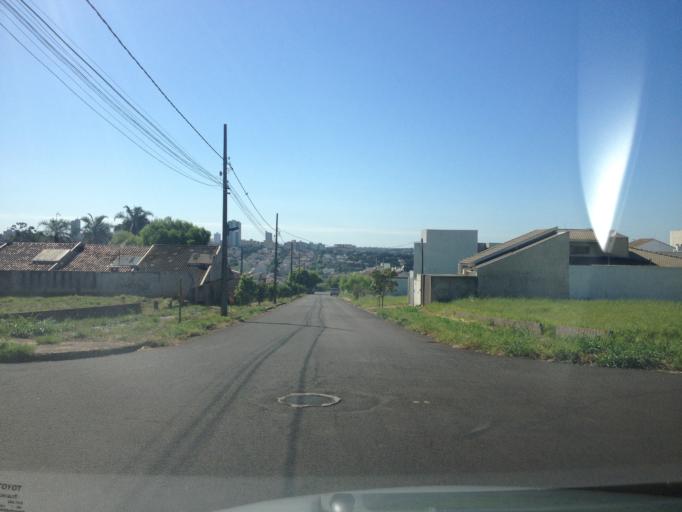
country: BR
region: Parana
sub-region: Maringa
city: Maringa
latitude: -23.4472
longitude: -51.9475
